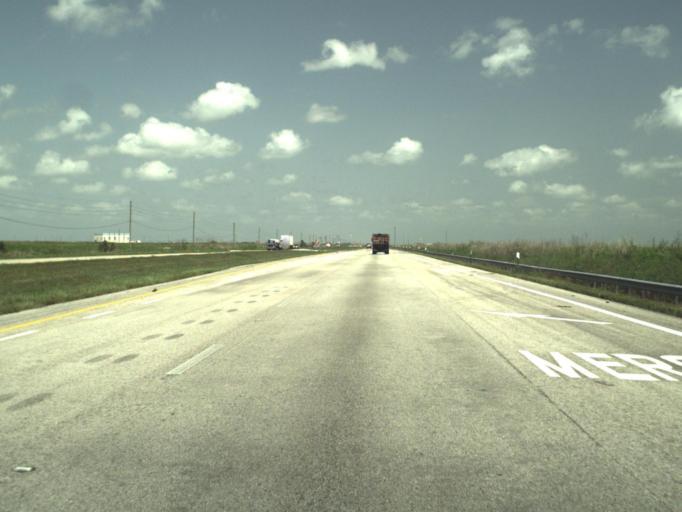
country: US
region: Florida
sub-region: Palm Beach County
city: Belle Glade Camp
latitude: 26.3868
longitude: -80.5777
